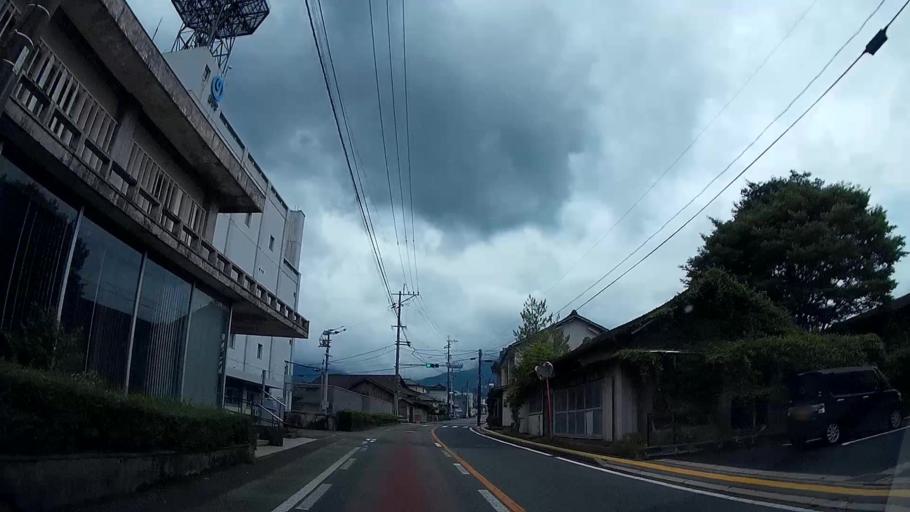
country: JP
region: Kumamoto
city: Aso
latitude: 32.9466
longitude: 131.1179
